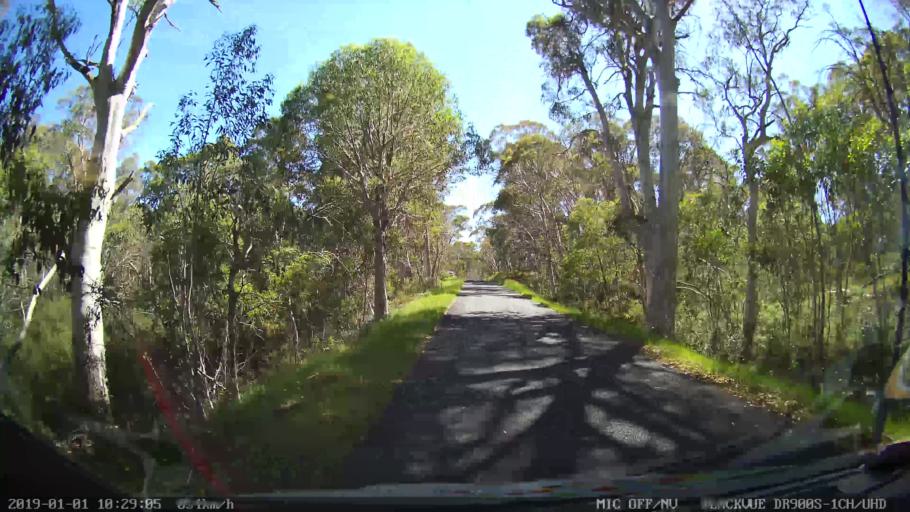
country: AU
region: New South Wales
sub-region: Snowy River
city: Jindabyne
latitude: -36.0565
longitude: 148.2452
